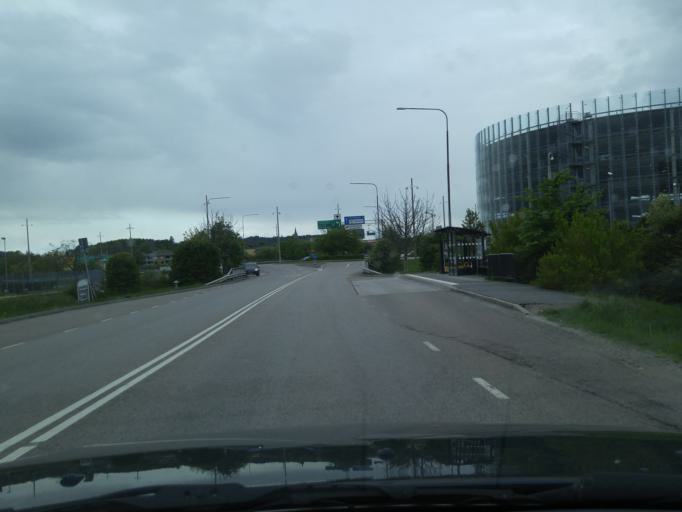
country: SE
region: Vaestra Goetaland
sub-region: Molndal
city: Moelndal
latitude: 57.6434
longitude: 12.0178
